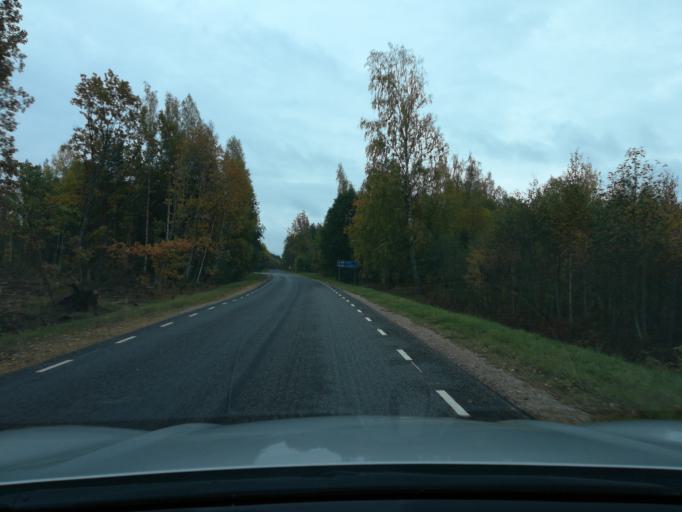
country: EE
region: Ida-Virumaa
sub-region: Johvi vald
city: Johvi
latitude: 59.0162
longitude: 27.4122
